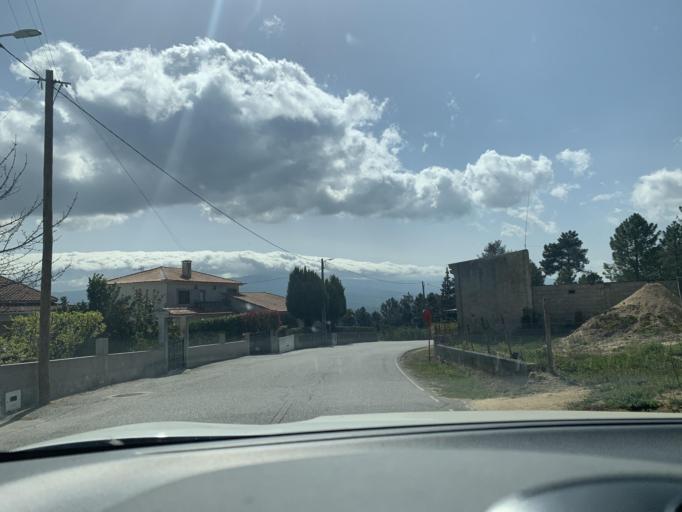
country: PT
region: Guarda
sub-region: Fornos de Algodres
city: Fornos de Algodres
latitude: 40.6076
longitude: -7.6033
